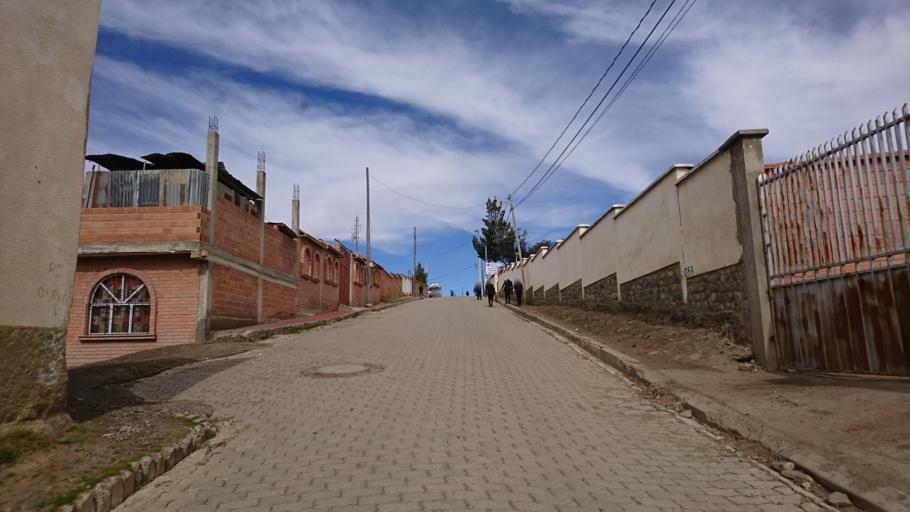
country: BO
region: La Paz
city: Batallas
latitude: -16.4008
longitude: -68.4783
